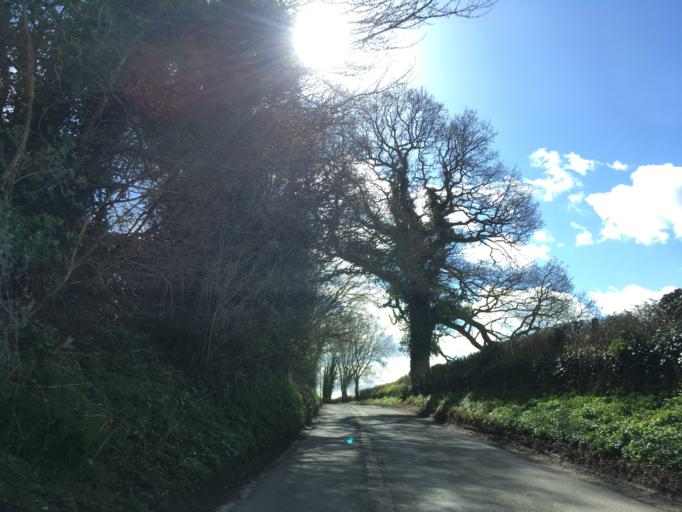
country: GB
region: England
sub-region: Gloucestershire
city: Wotton-under-Edge
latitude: 51.6294
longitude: -2.3441
